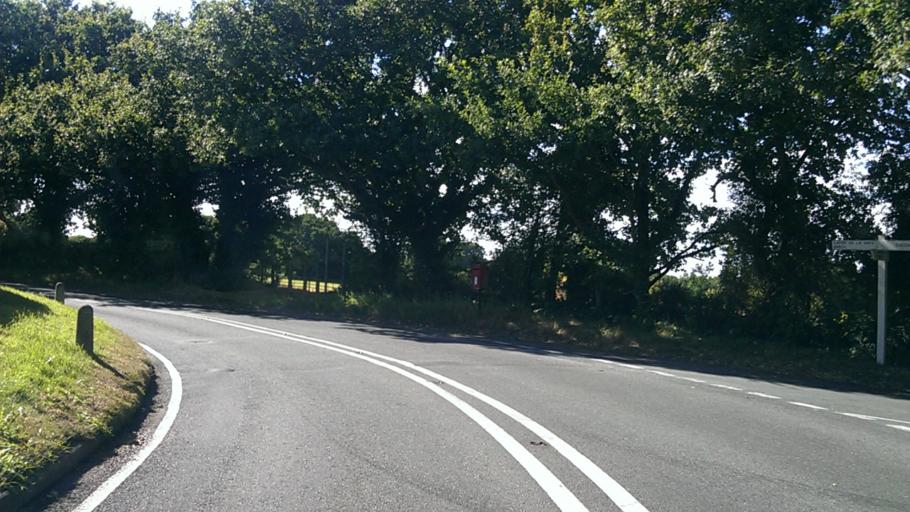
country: GB
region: England
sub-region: Essex
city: Layer de la Haye
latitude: 51.8465
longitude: 0.8786
